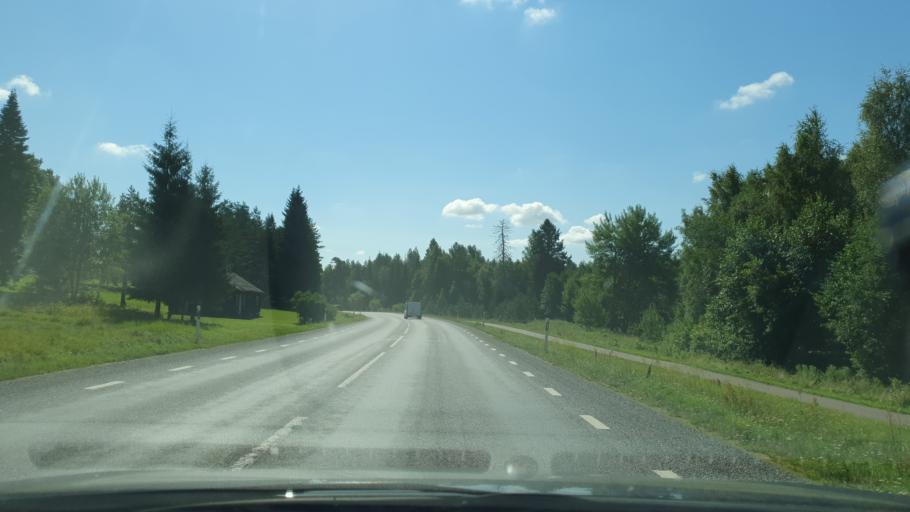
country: EE
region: Harju
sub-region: Kuusalu vald
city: Kuusalu
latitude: 59.2587
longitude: 25.6631
